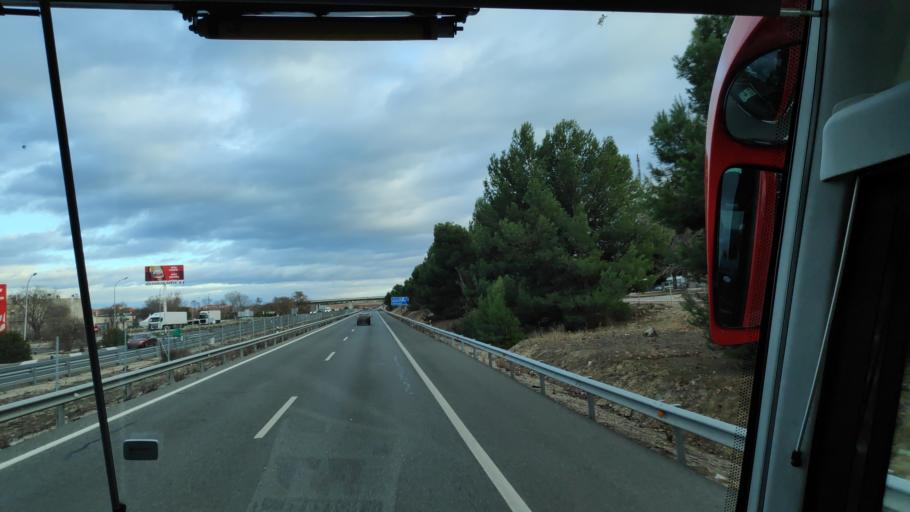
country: ES
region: Madrid
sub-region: Provincia de Madrid
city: Villarejo de Salvanes
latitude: 40.1676
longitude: -3.2862
